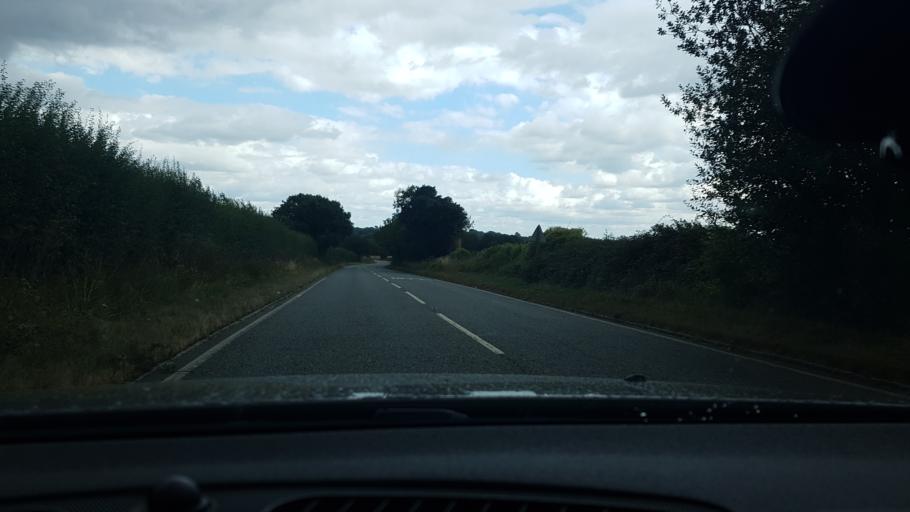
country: GB
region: England
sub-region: West Berkshire
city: Wickham
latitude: 51.4513
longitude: -1.4584
